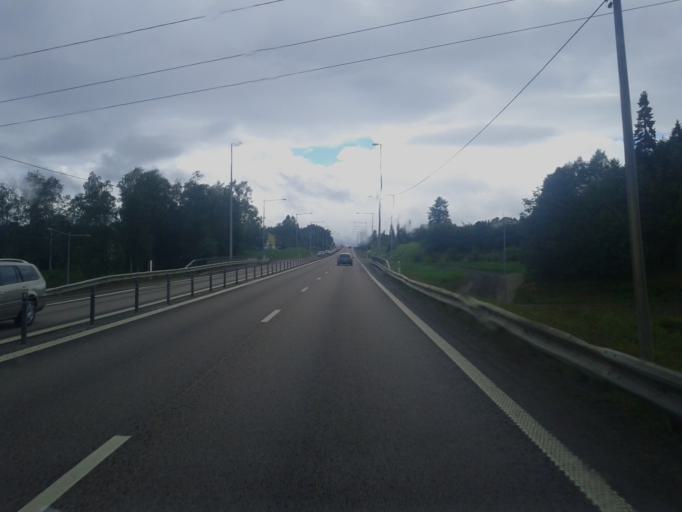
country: SE
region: Vaesternorrland
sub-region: Haernoesands Kommun
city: Haernoesand
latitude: 62.6439
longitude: 17.9089
